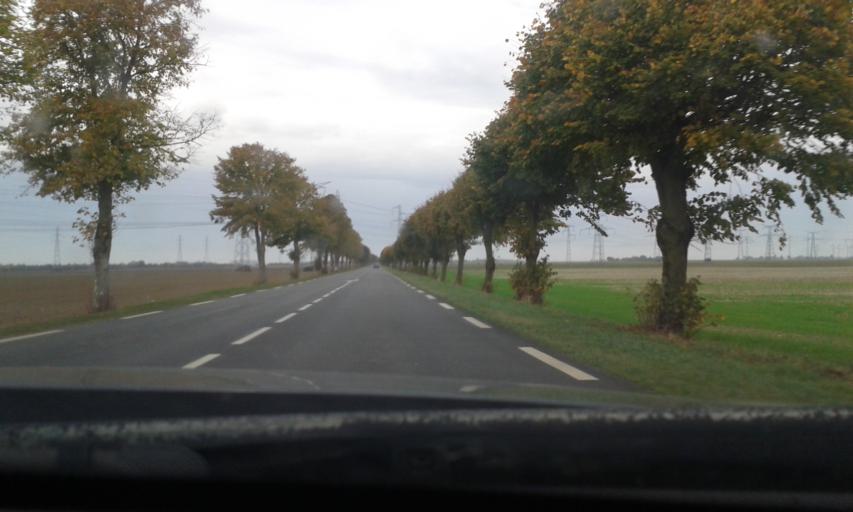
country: FR
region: Centre
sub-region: Departement du Loiret
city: Artenay
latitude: 48.1103
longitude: 1.8623
